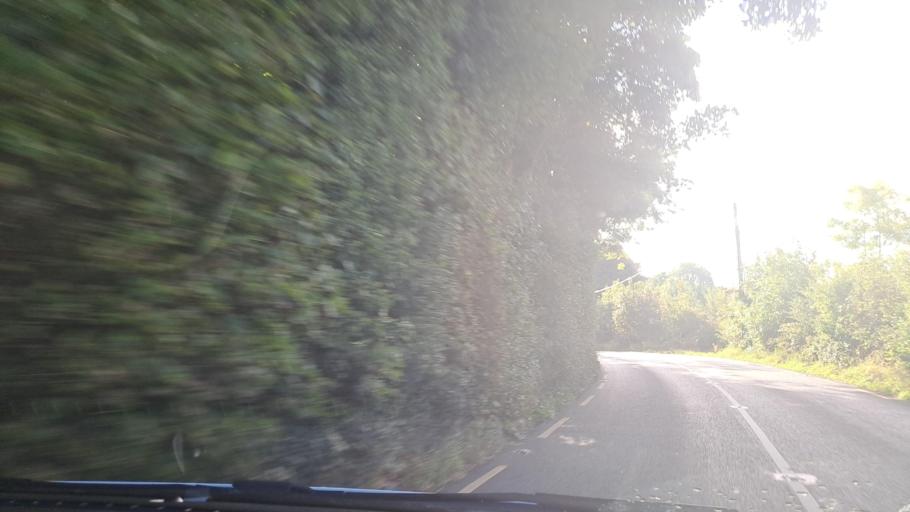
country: IE
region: Ulster
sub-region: County Monaghan
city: Carrickmacross
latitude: 53.9916
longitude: -6.7729
